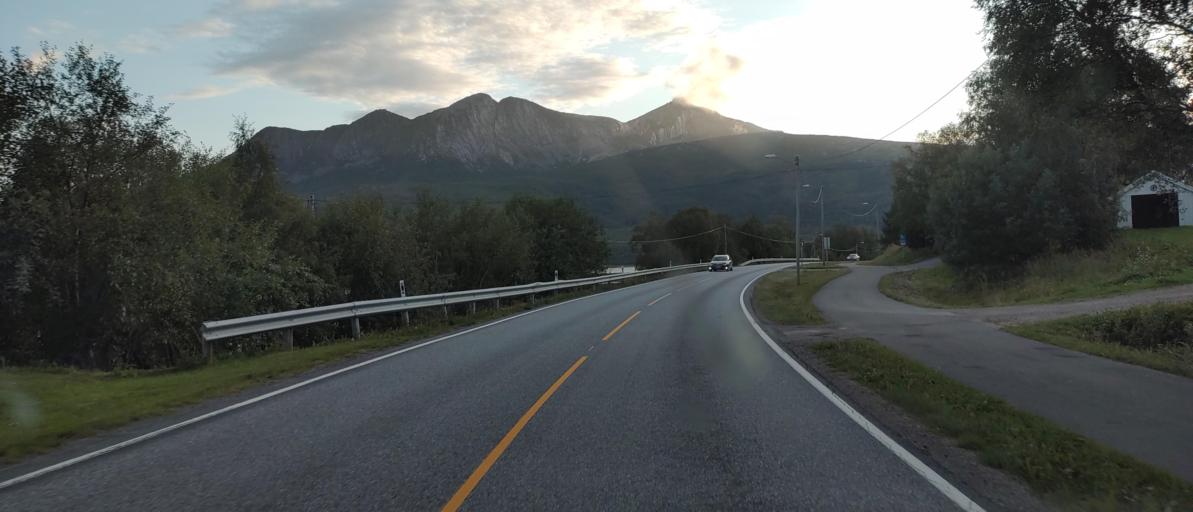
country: NO
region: Nordland
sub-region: Lodingen
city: Lodingen
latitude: 68.1936
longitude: 16.0543
